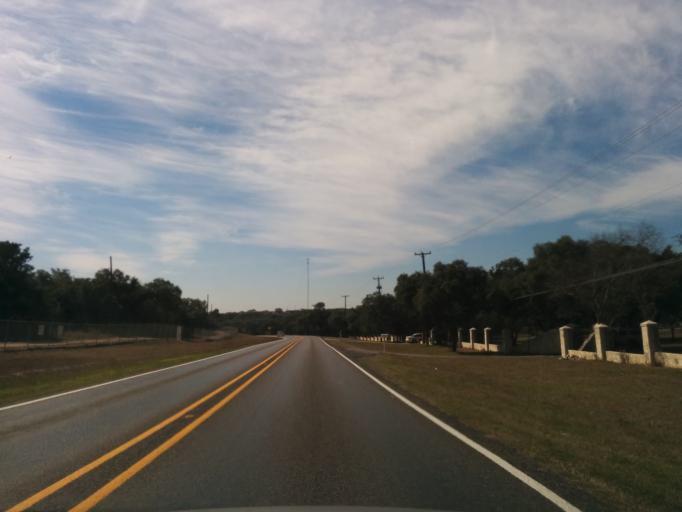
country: US
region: Texas
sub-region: Bexar County
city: Fair Oaks Ranch
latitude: 29.7160
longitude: -98.6254
